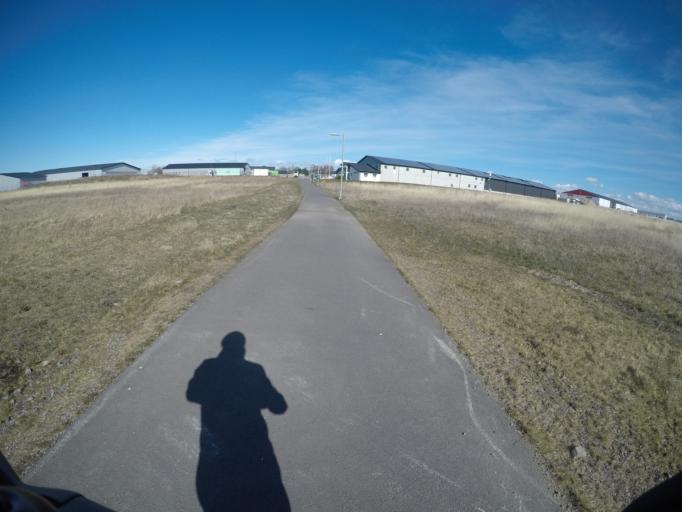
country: SE
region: Halland
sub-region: Laholms Kommun
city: Laholm
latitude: 56.4980
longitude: 13.0070
